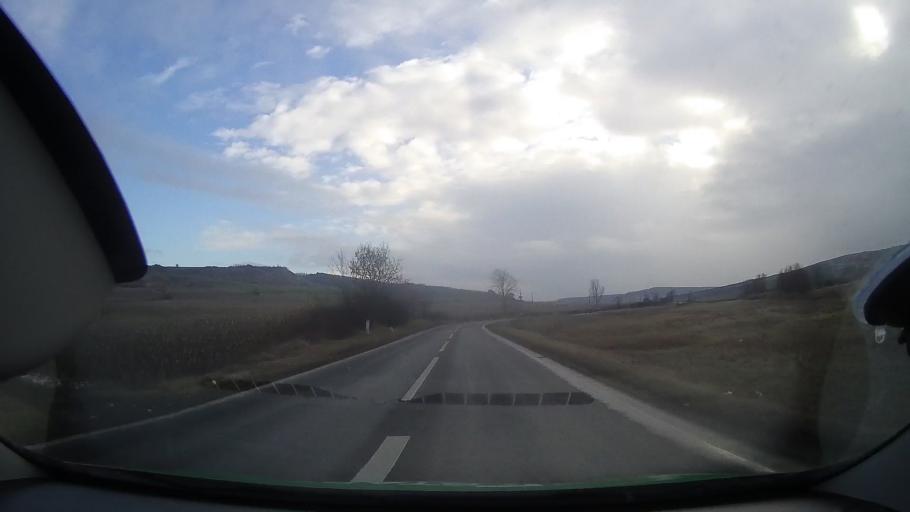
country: RO
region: Mures
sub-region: Comuna Cucerdea
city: Cucerdea
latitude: 46.3827
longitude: 24.2551
